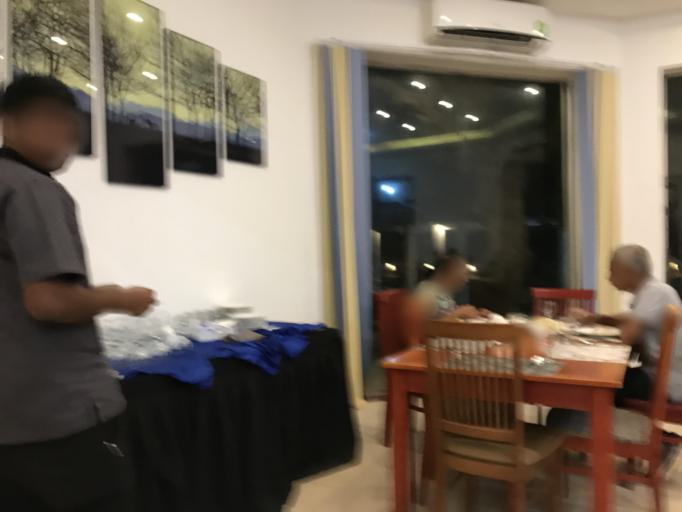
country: LK
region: Northern Province
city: Valvedditturai
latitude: 9.8161
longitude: 80.0484
